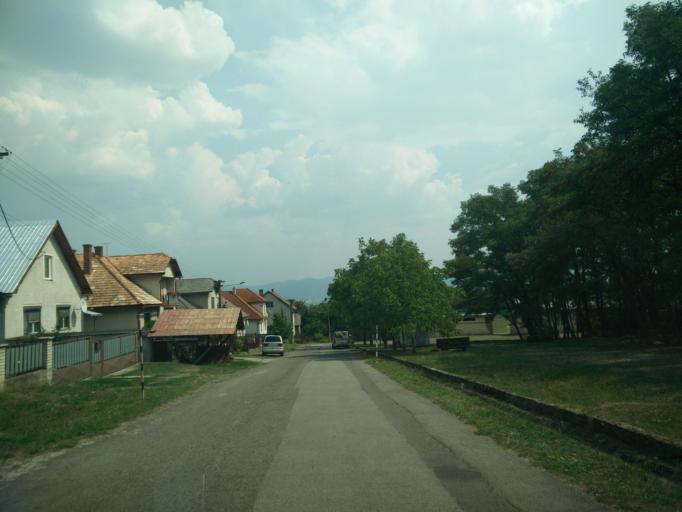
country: SK
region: Banskobystricky
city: Ziar nad Hronom
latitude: 48.5907
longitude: 18.7541
